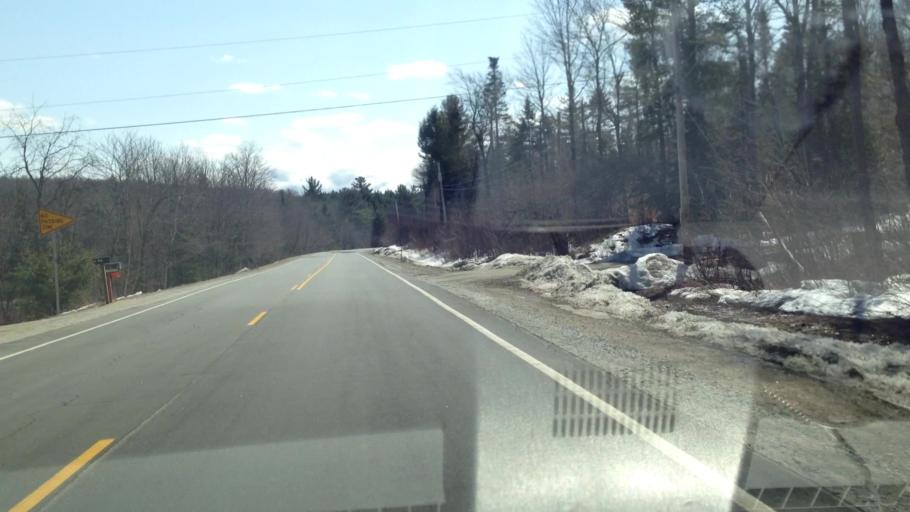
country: US
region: New Hampshire
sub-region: Merrimack County
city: Wilmot
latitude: 43.4750
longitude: -71.9653
